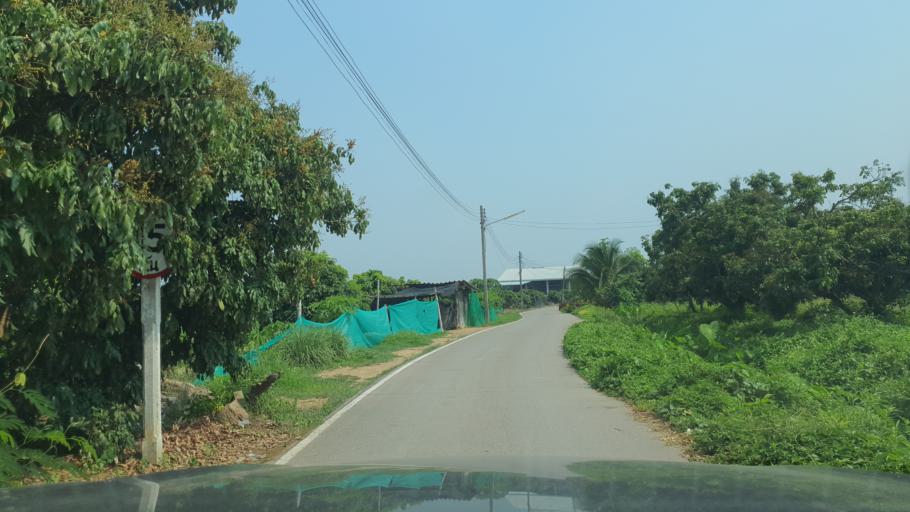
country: TH
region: Chiang Mai
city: Hang Dong
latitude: 18.6542
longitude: 98.9878
